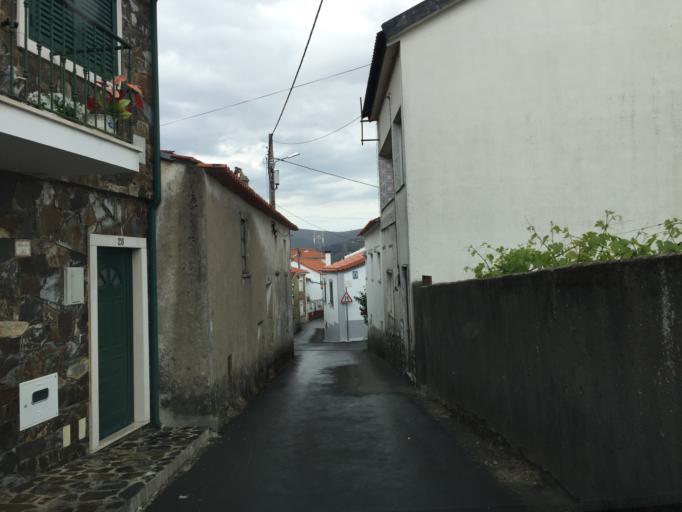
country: PT
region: Coimbra
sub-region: Pampilhosa da Serra
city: Pampilhosa da Serra
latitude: 40.0423
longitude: -8.0031
